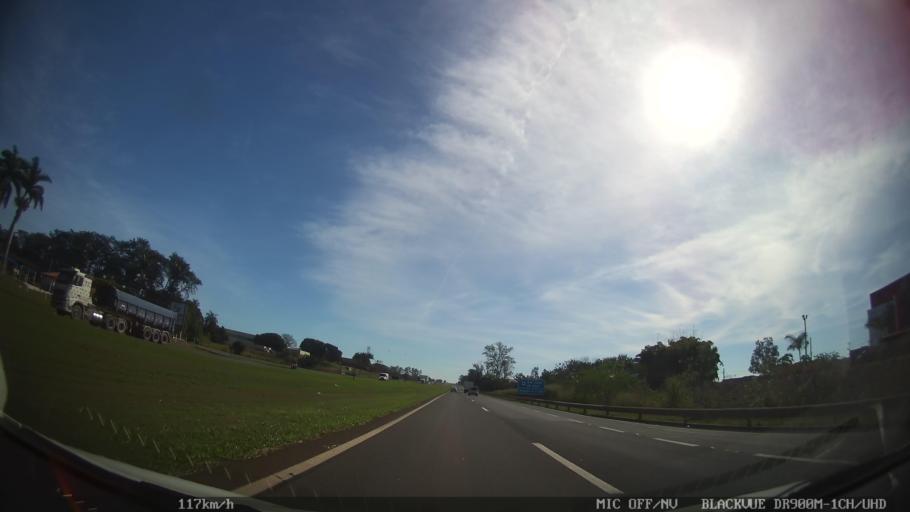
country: BR
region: Sao Paulo
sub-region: Leme
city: Leme
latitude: -22.2166
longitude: -47.3928
